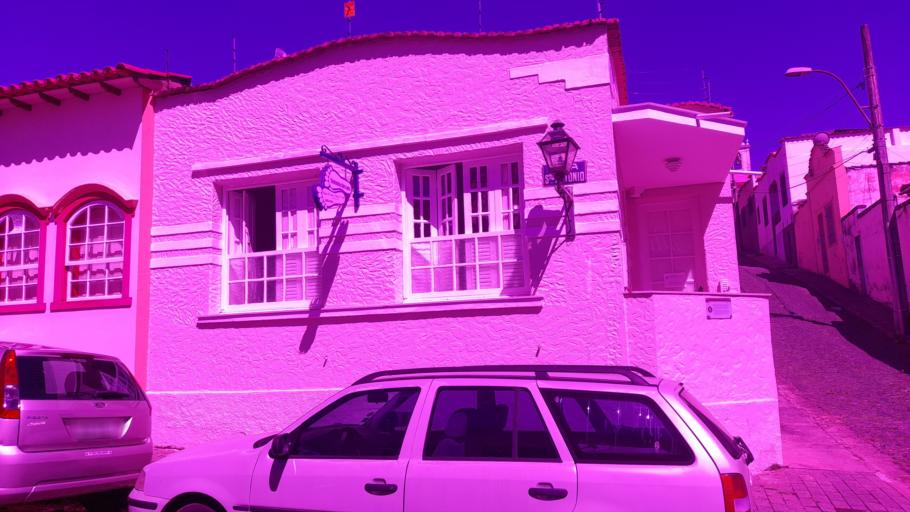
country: BR
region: Minas Gerais
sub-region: Sao Joao Del Rei
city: Sao Joao del Rei
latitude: -21.1367
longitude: -44.2631
